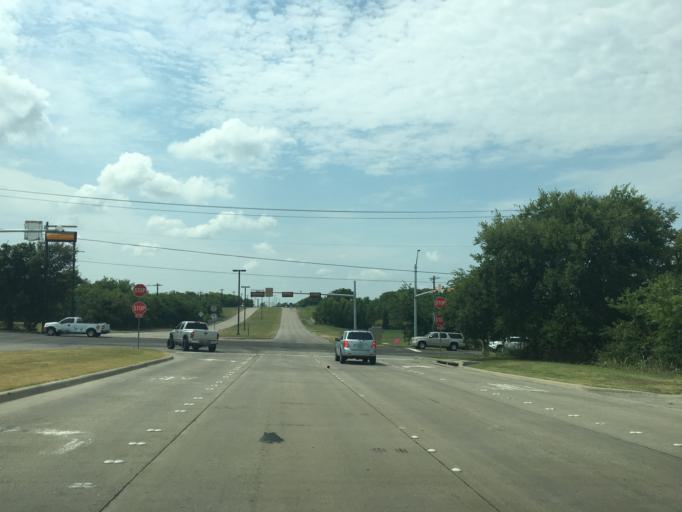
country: US
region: Texas
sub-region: Rockwall County
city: Rockwall
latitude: 32.9662
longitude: -96.4526
